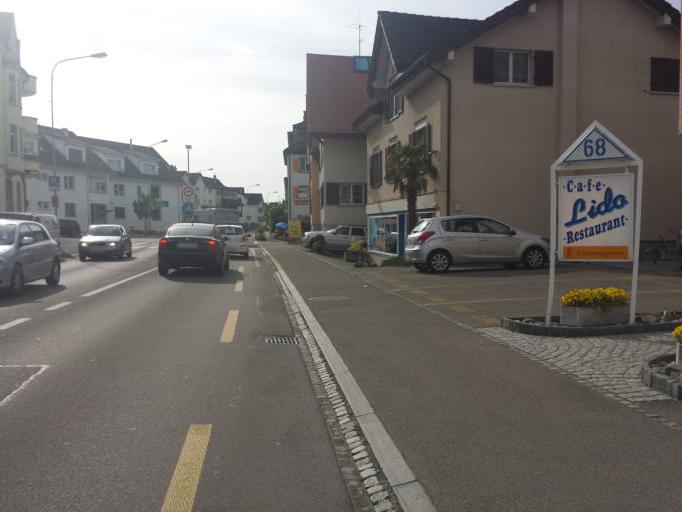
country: CH
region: Saint Gallen
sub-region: Wahlkreis Rorschach
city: Horn
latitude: 47.4958
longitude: 9.4634
